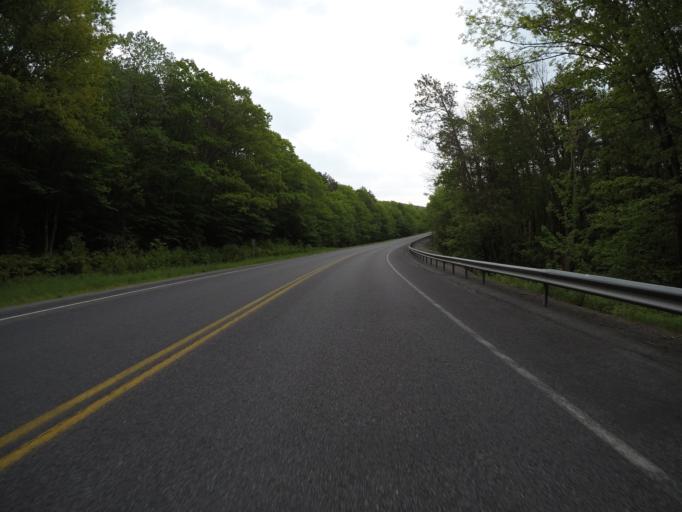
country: US
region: New York
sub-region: Sullivan County
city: Livingston Manor
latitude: 42.0476
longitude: -74.9097
